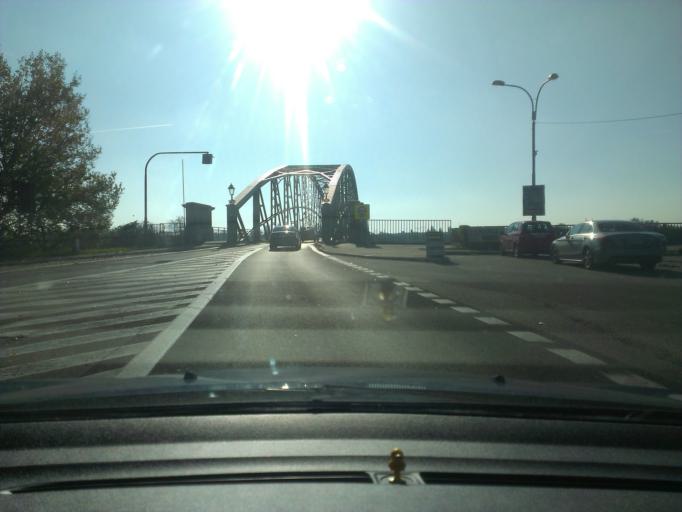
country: SK
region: Nitriansky
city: Komarno
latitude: 47.7535
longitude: 18.1213
